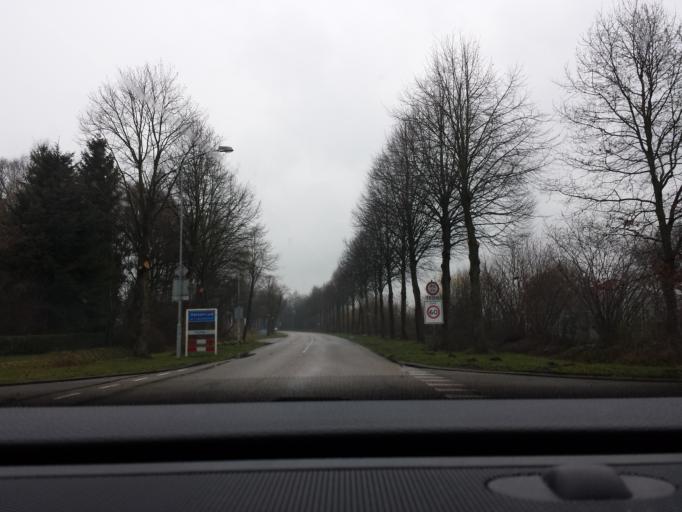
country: NL
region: Gelderland
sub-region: Oude IJsselstreek
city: Varsseveld
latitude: 51.9474
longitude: 6.4591
